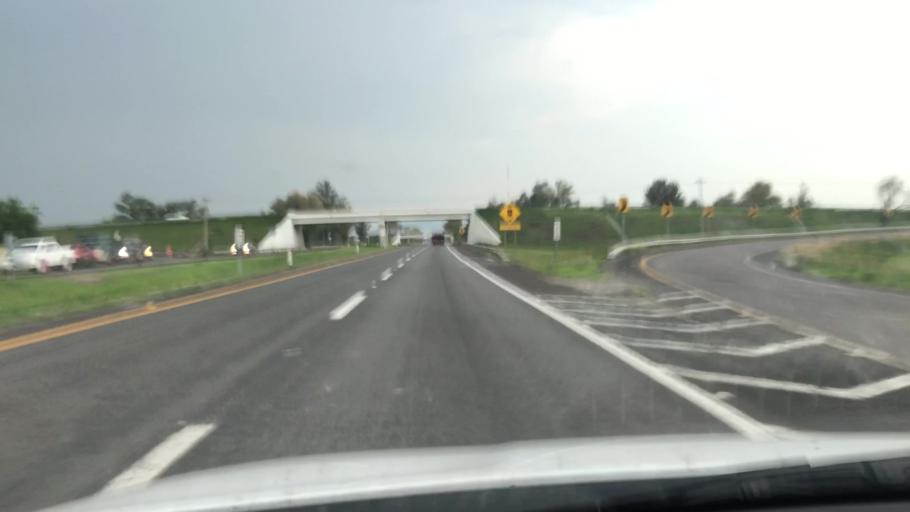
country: MX
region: Jalisco
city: La Barca
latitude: 20.3221
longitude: -102.5348
